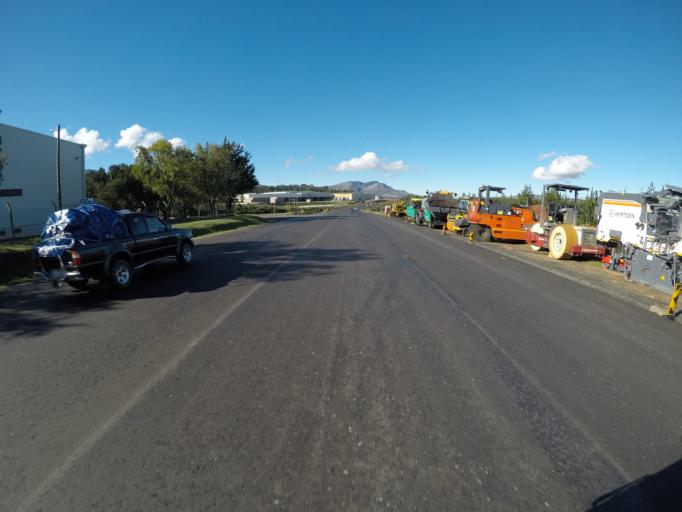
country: ZA
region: Western Cape
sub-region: Overberg District Municipality
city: Grabouw
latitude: -34.1783
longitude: 19.0727
